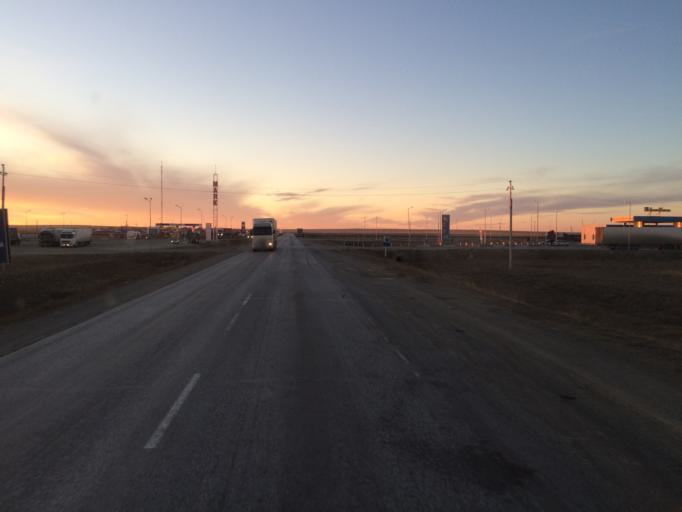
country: RU
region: Orenburg
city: Dombarovskiy
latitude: 49.9691
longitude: 60.0656
